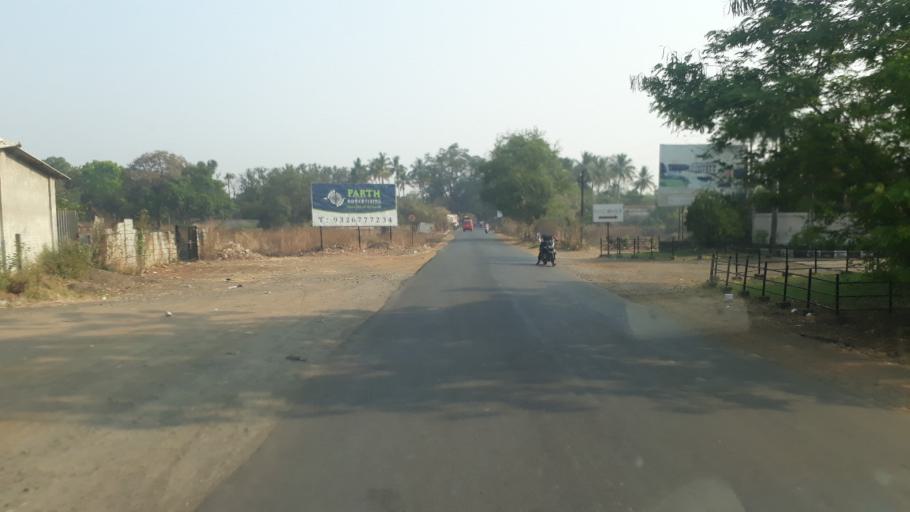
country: IN
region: Maharashtra
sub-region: Raigarh
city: Neral
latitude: 19.0360
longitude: 73.3276
